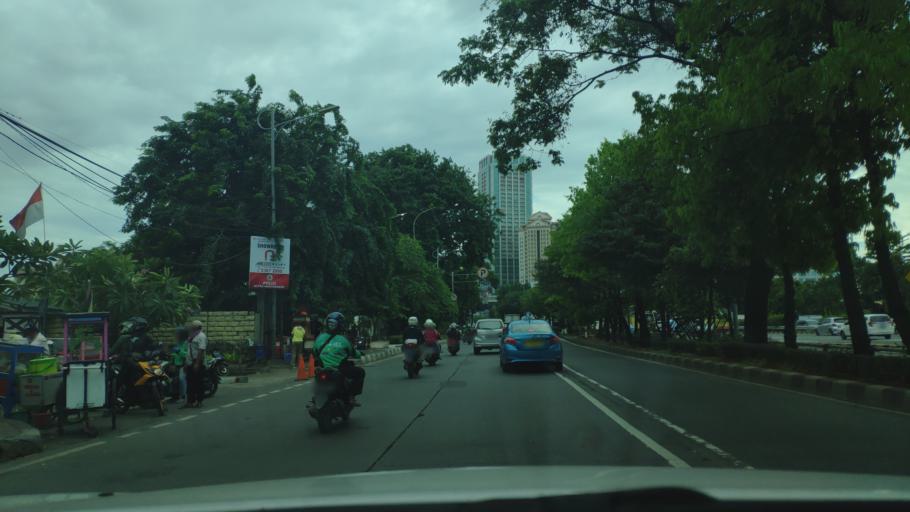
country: ID
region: Jakarta Raya
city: Jakarta
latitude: -6.1952
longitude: 106.7977
